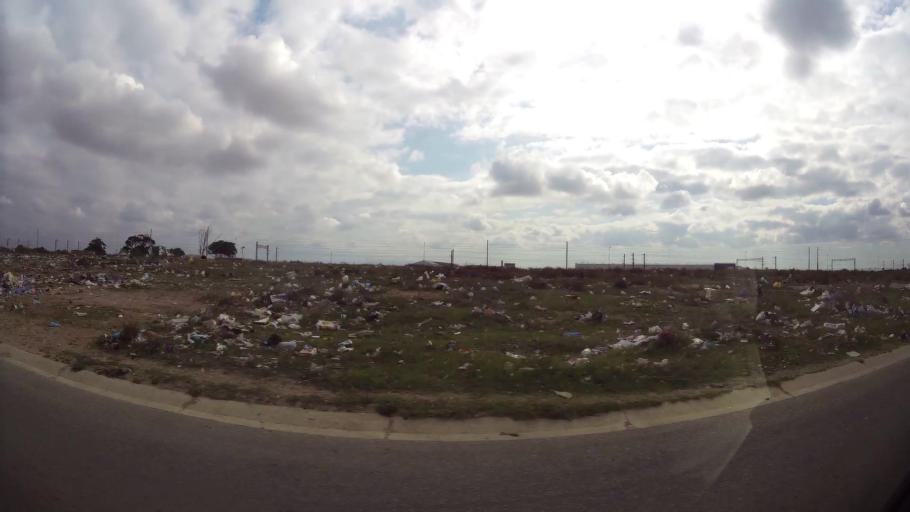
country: ZA
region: Eastern Cape
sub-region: Nelson Mandela Bay Metropolitan Municipality
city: Port Elizabeth
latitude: -33.8184
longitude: 25.6306
